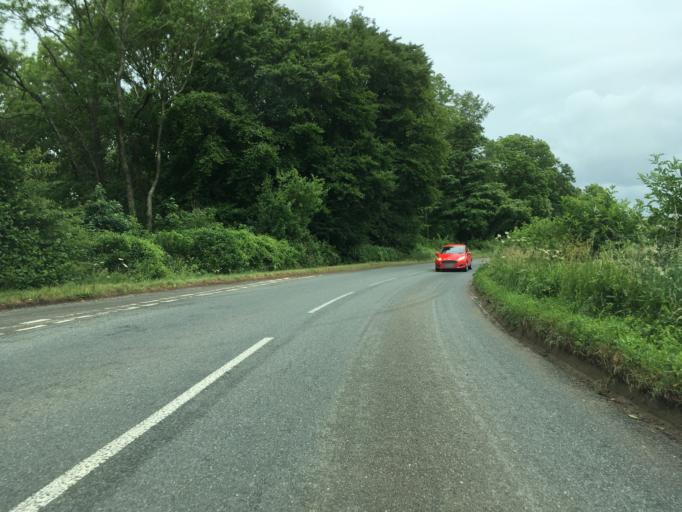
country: GB
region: England
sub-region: Gloucestershire
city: Chipping Campden
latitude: 52.0463
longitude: -1.8120
